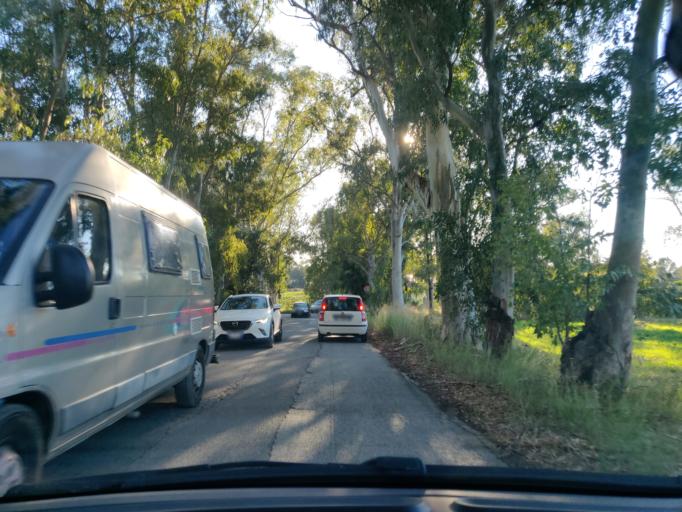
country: IT
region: Latium
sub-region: Citta metropolitana di Roma Capitale
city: Aurelia
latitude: 42.1506
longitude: 11.7487
